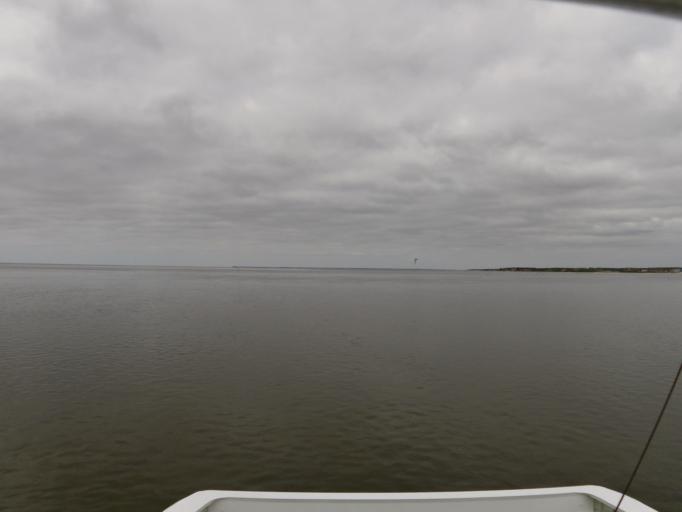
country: DE
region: Schleswig-Holstein
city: Langeness
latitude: 54.6758
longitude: 8.6013
